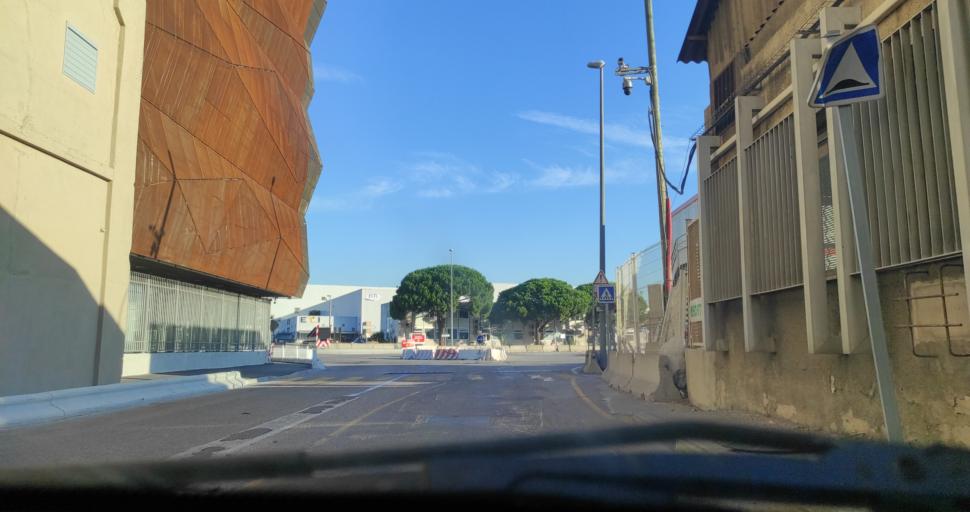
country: FR
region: Provence-Alpes-Cote d'Azur
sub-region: Departement des Bouches-du-Rhone
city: Marseille 16
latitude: 43.3394
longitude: 5.3461
